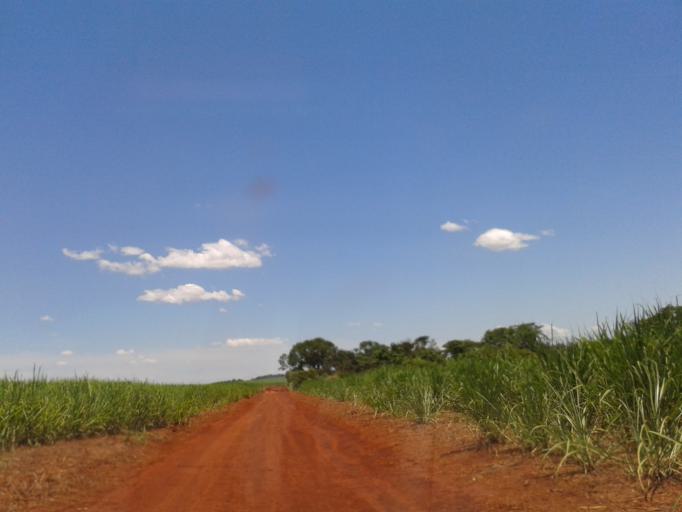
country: BR
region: Minas Gerais
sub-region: Centralina
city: Centralina
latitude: -18.6654
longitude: -49.2394
